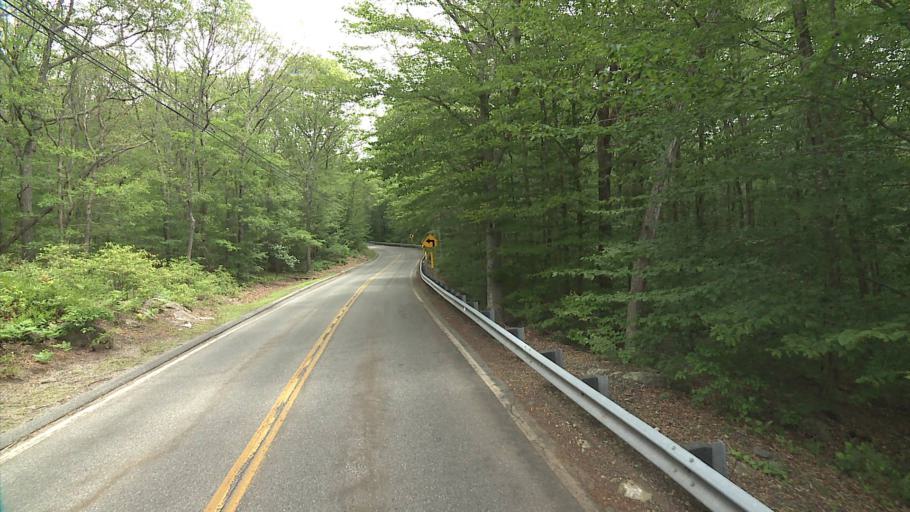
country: US
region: Connecticut
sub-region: New London County
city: Ledyard Center
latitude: 41.4513
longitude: -71.9729
